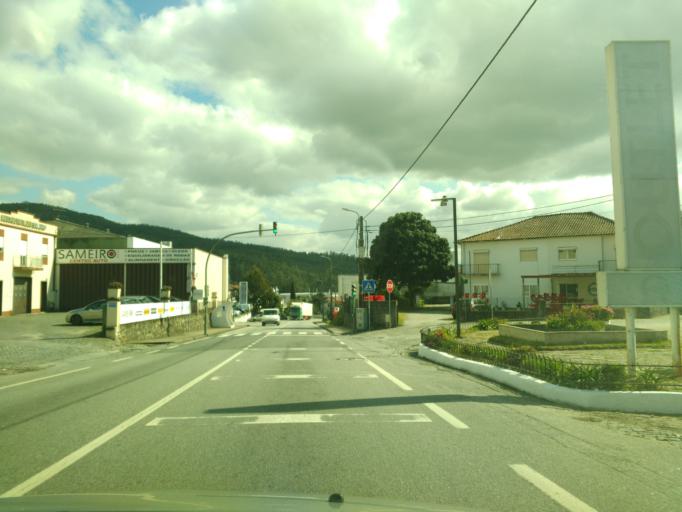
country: PT
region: Braga
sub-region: Braga
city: Braga
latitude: 41.5293
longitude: -8.4181
